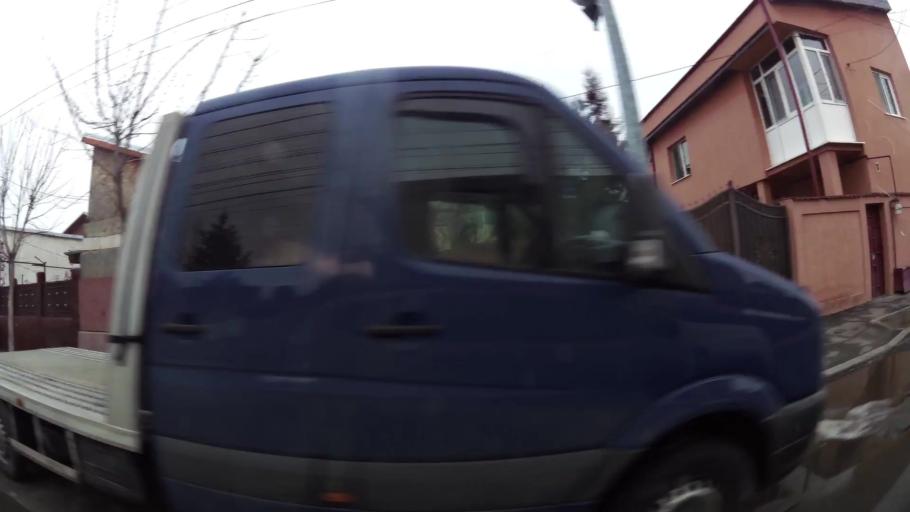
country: RO
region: Ilfov
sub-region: Voluntari City
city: Voluntari
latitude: 44.4811
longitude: 26.1754
